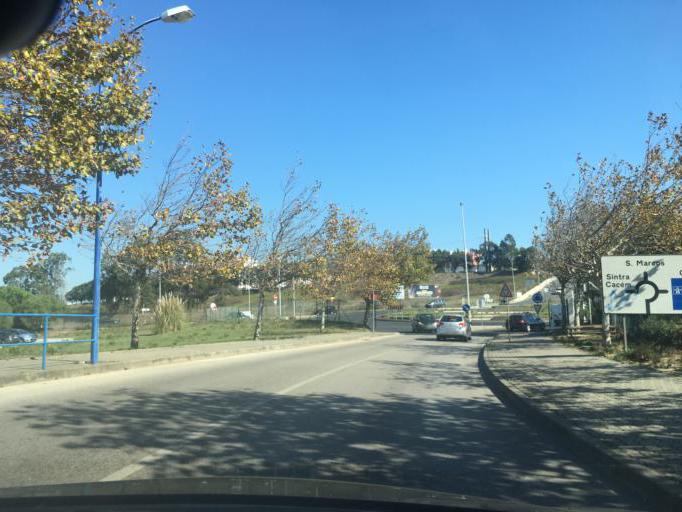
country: PT
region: Lisbon
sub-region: Sintra
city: Cacem
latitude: 38.7465
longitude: -9.3048
